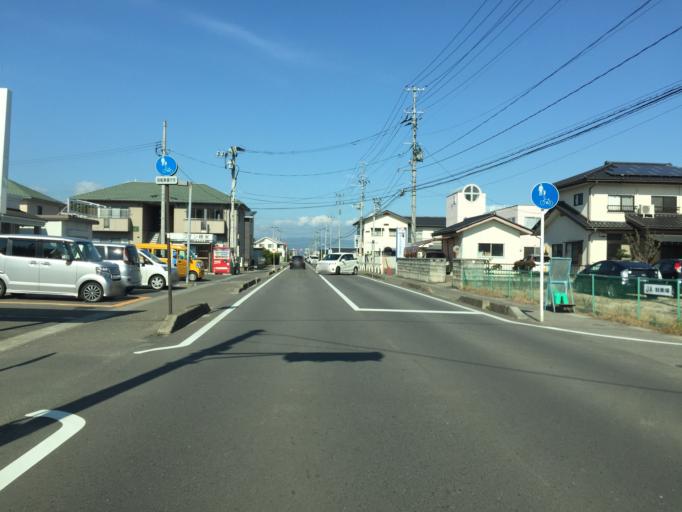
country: JP
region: Fukushima
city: Fukushima-shi
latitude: 37.7749
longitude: 140.5011
